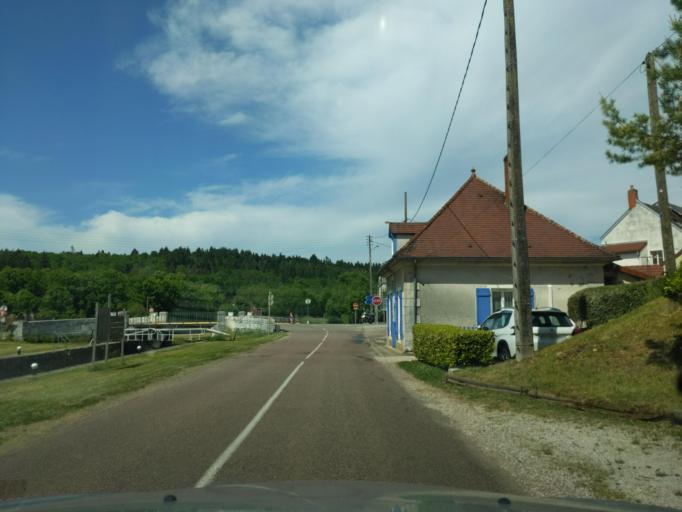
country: FR
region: Bourgogne
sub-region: Departement de la Cote-d'Or
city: Fleurey-sur-Ouche
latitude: 47.2965
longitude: 4.8148
